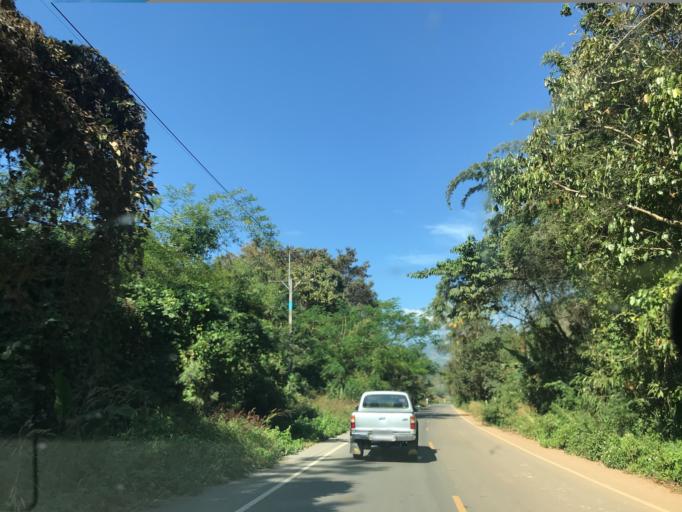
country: TH
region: Chiang Rai
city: Mae Lao
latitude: 19.8064
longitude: 99.6477
